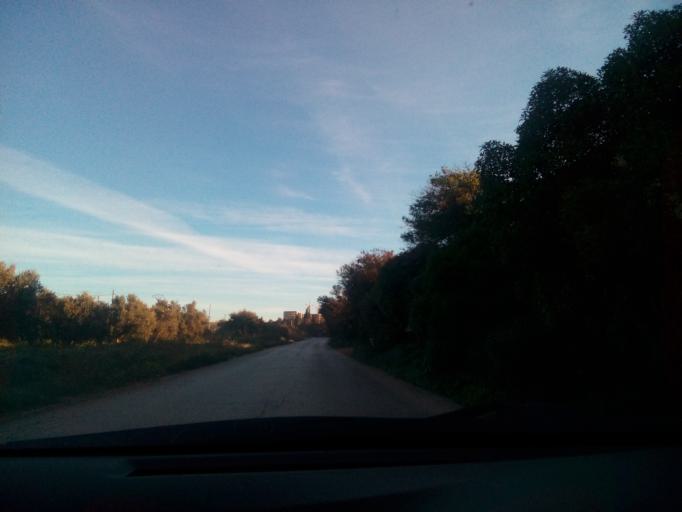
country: DZ
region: Oran
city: Es Senia
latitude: 35.6213
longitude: -0.6805
